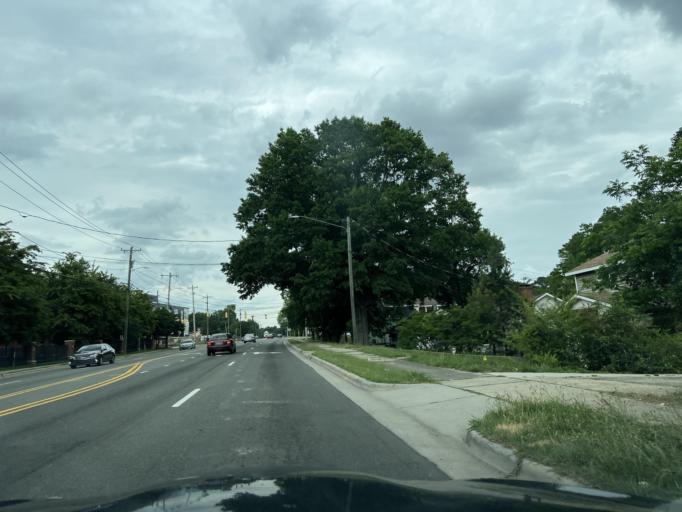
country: US
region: North Carolina
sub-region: Durham County
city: Durham
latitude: 35.9742
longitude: -78.8937
